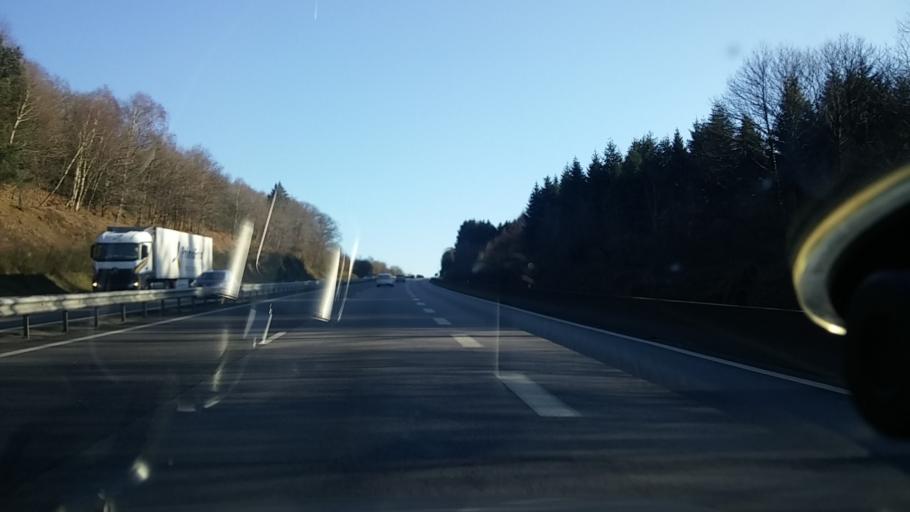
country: FR
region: Limousin
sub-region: Departement de la Haute-Vienne
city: Razes
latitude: 46.0666
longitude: 1.3610
